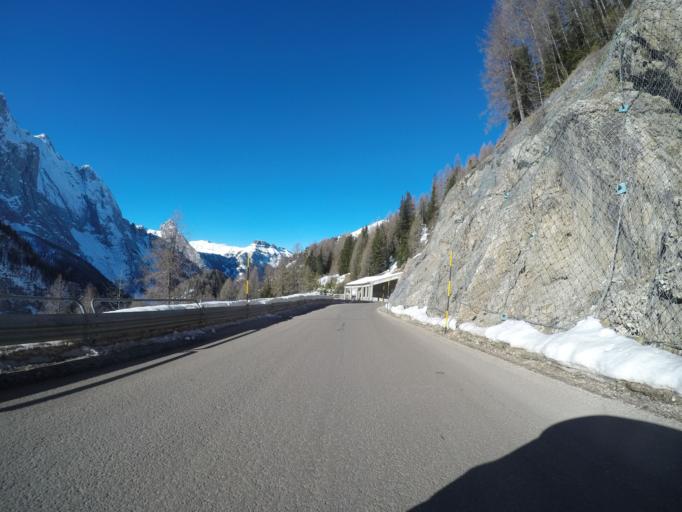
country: IT
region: Trentino-Alto Adige
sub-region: Provincia di Trento
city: Canazei
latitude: 46.4675
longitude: 11.8494
